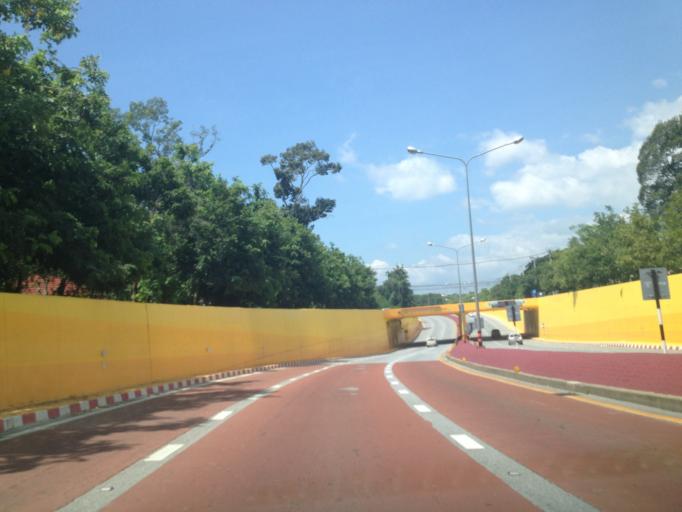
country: TH
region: Chiang Mai
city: Saraphi
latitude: 18.7443
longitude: 99.0150
